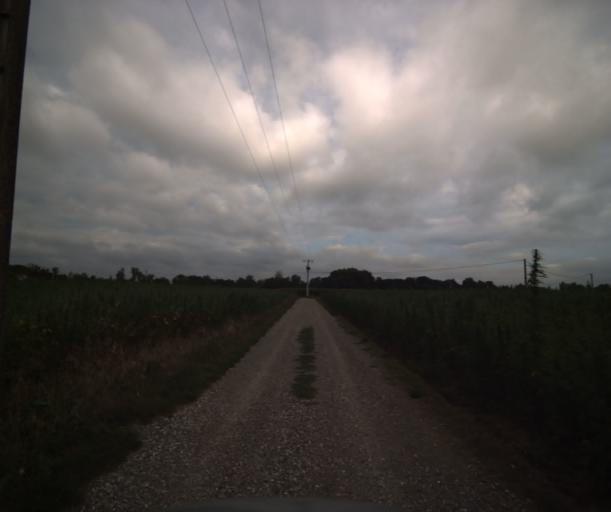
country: FR
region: Midi-Pyrenees
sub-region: Departement de la Haute-Garonne
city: Labastidette
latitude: 43.4463
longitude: 1.2875
